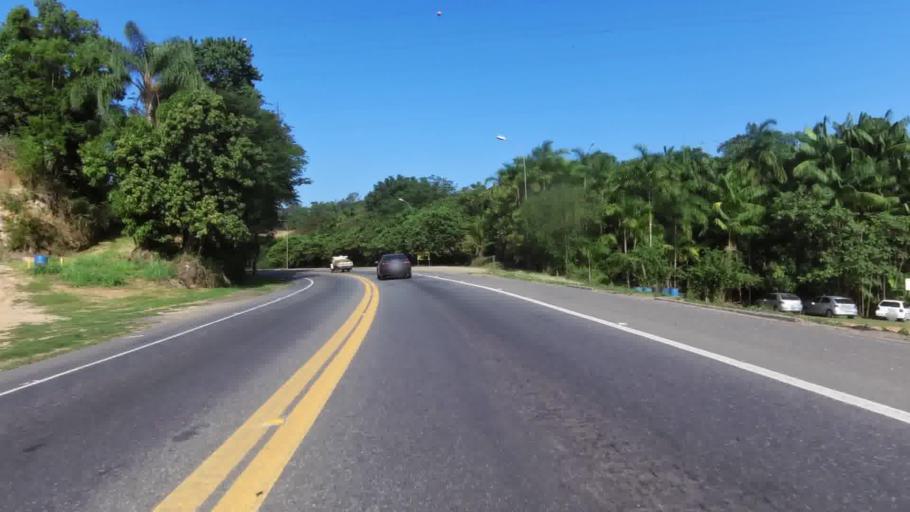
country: BR
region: Espirito Santo
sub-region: Iconha
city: Iconha
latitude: -20.7882
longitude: -40.7965
